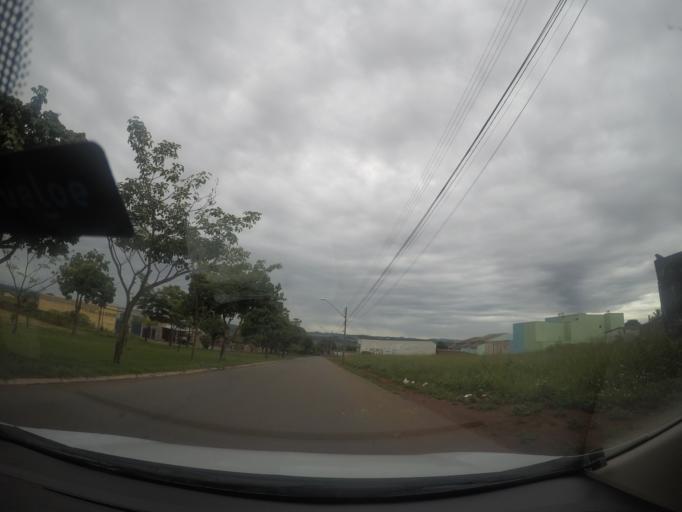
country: BR
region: Goias
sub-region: Goiania
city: Goiania
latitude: -16.6068
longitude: -49.3043
